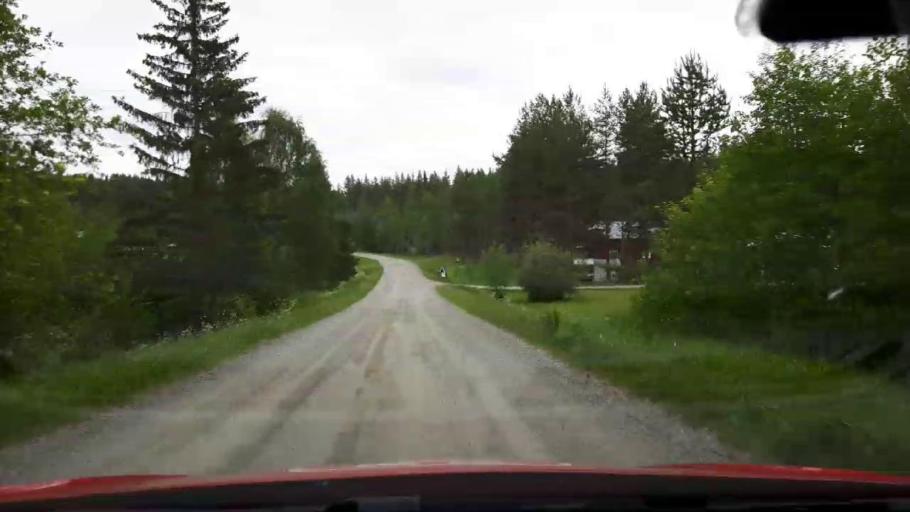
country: SE
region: Jaemtland
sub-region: Ragunda Kommun
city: Hammarstrand
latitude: 63.2017
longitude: 16.1235
